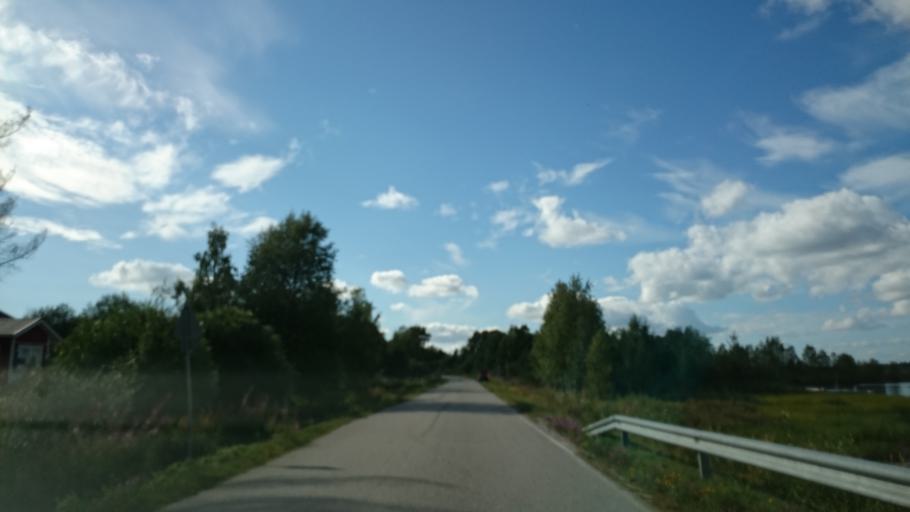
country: FI
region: Kainuu
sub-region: Kehys-Kainuu
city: Suomussalmi
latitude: 64.7364
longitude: 29.4474
